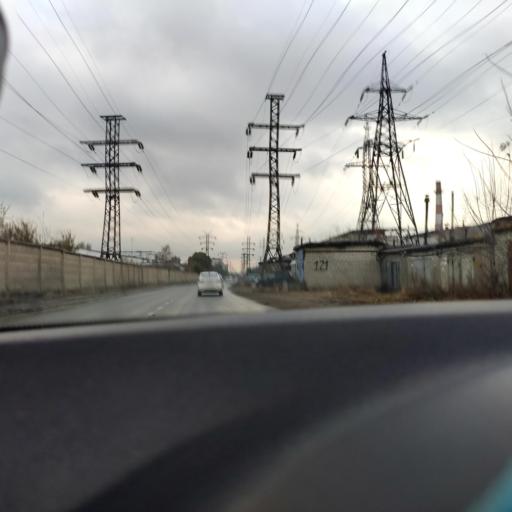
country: RU
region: Samara
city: Petra-Dubrava
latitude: 53.2450
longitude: 50.2919
